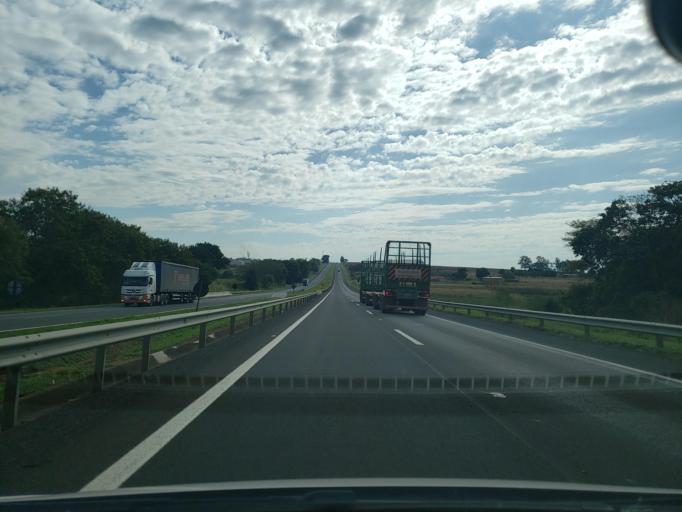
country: BR
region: Sao Paulo
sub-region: Lins
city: Lins
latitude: -21.6488
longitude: -49.8141
